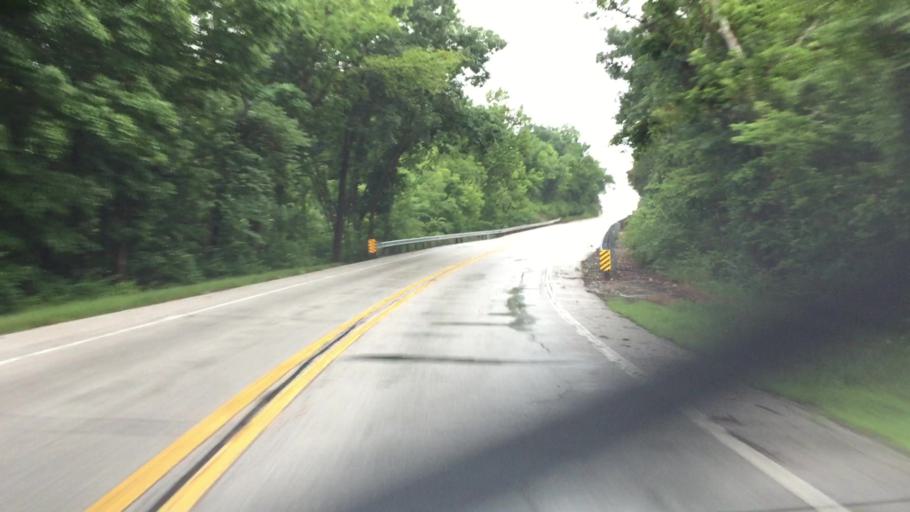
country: US
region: Illinois
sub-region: Hancock County
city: Nauvoo
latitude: 40.5172
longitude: -91.3589
